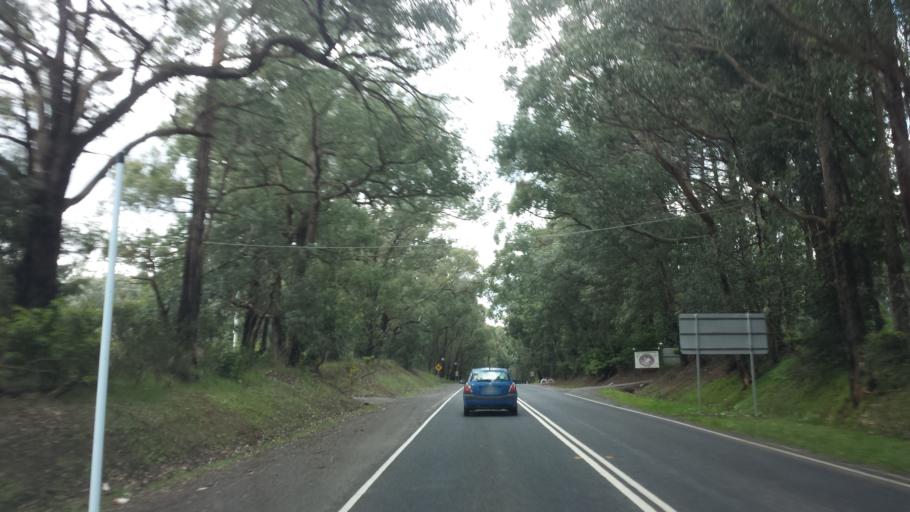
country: AU
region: Victoria
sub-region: Yarra Ranges
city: Selby
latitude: -37.9376
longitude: 145.4040
